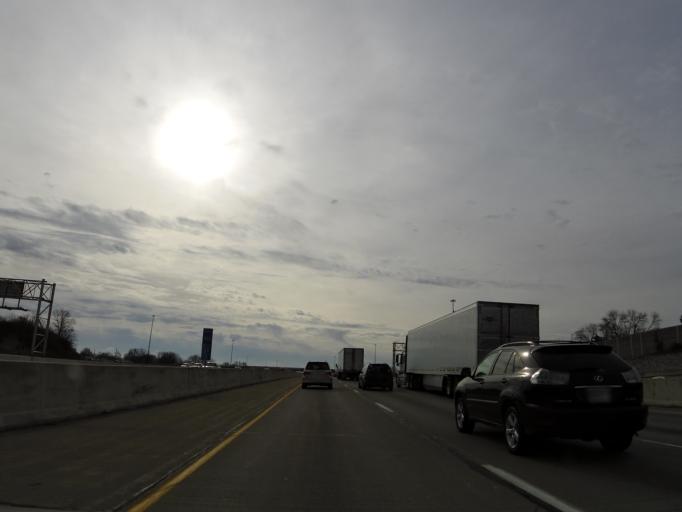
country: US
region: Indiana
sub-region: Marion County
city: Lawrence
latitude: 39.8589
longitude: -86.0471
